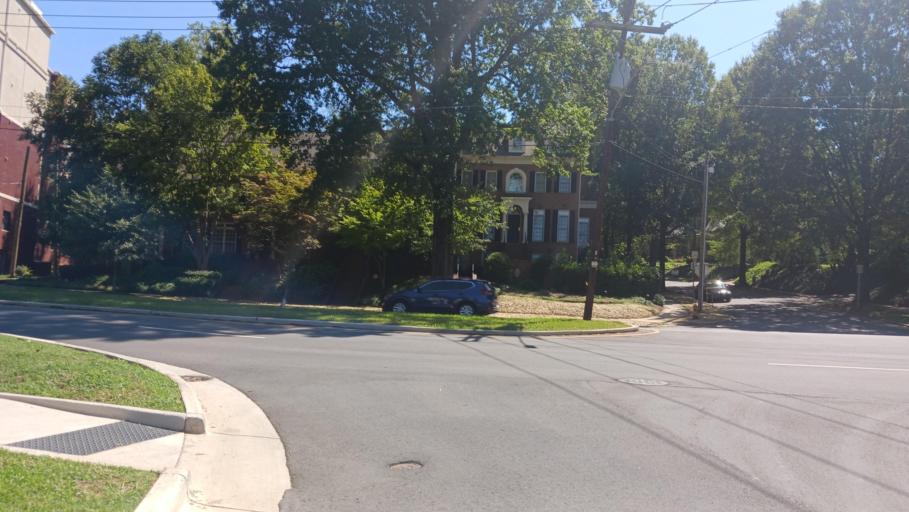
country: US
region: North Carolina
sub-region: Mecklenburg County
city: Charlotte
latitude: 35.2066
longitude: -80.8281
